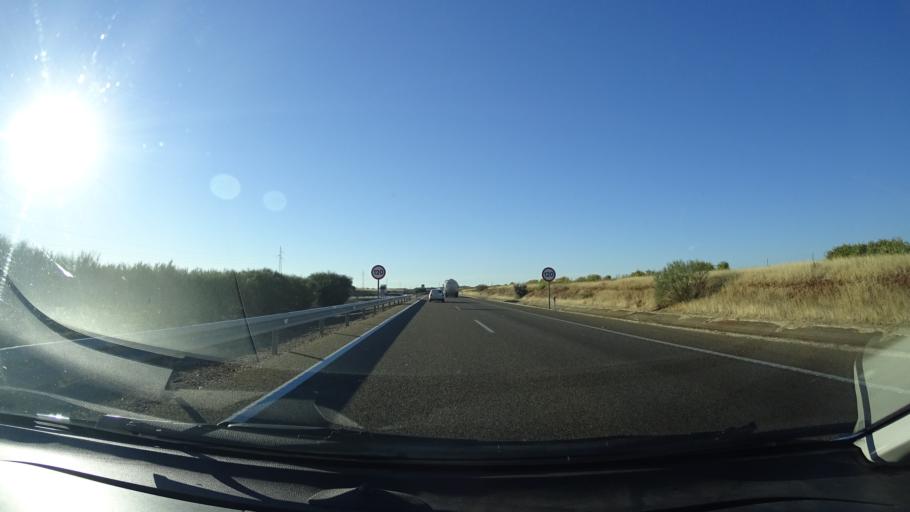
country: ES
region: Extremadura
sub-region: Provincia de Badajoz
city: Villafranca de los Barros
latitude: 38.5830
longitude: -6.3643
